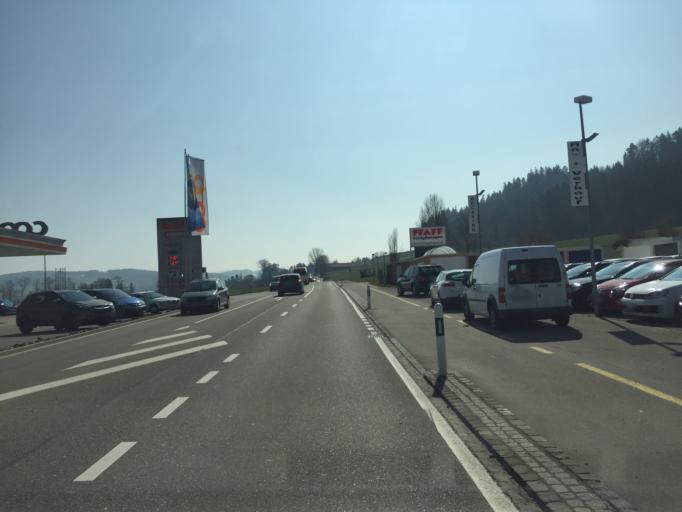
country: CH
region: Saint Gallen
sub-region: Wahlkreis Wil
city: Wil
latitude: 47.4388
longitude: 9.0561
